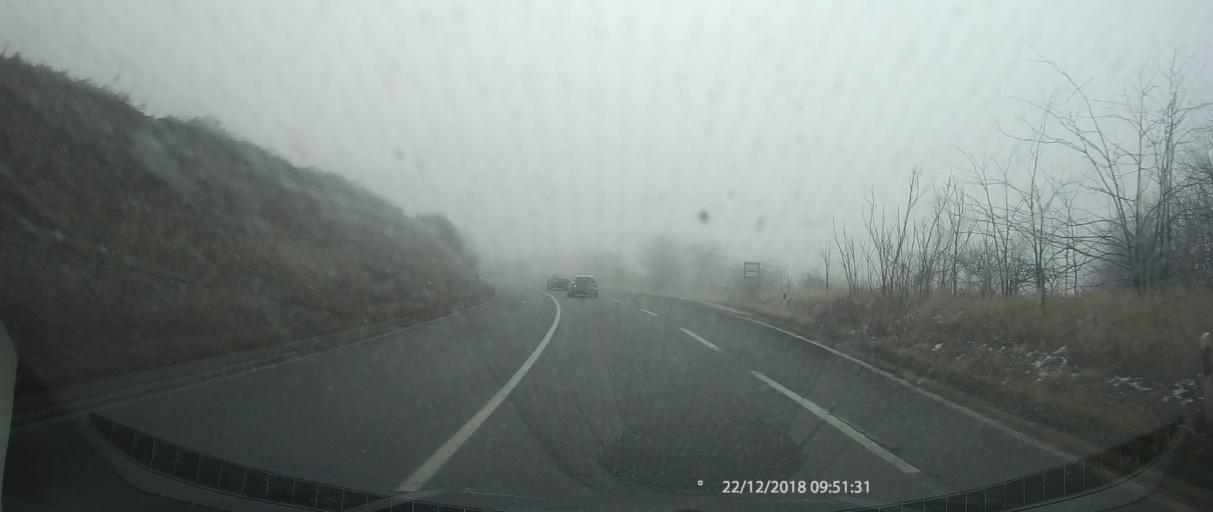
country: MK
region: Staro Nagoricane
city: Staro Nagorichane
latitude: 42.1697
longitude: 21.8067
